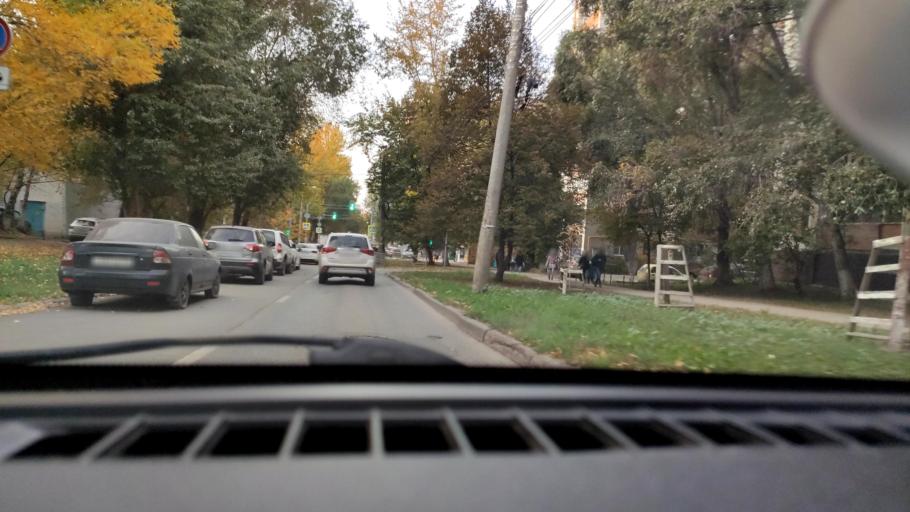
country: RU
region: Samara
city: Samara
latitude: 53.2133
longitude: 50.1636
